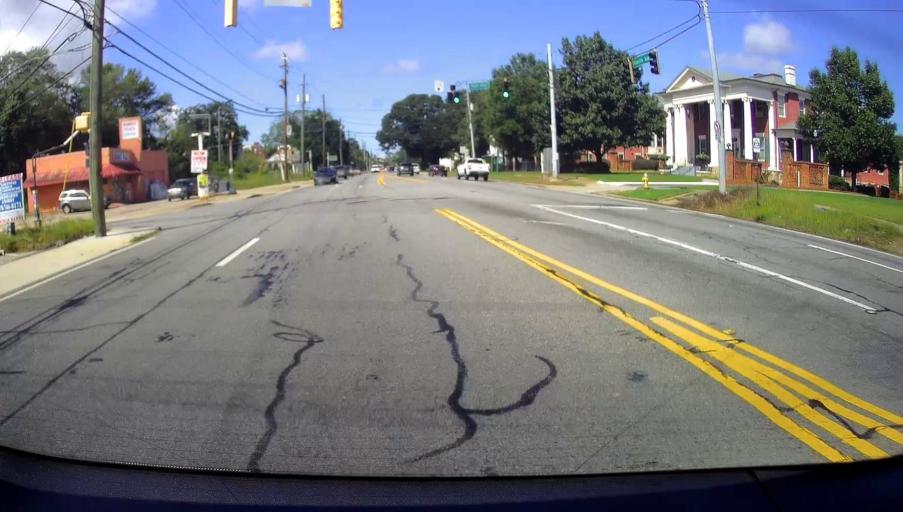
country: US
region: Georgia
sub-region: Bibb County
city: Macon
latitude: 32.8420
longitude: -83.6498
